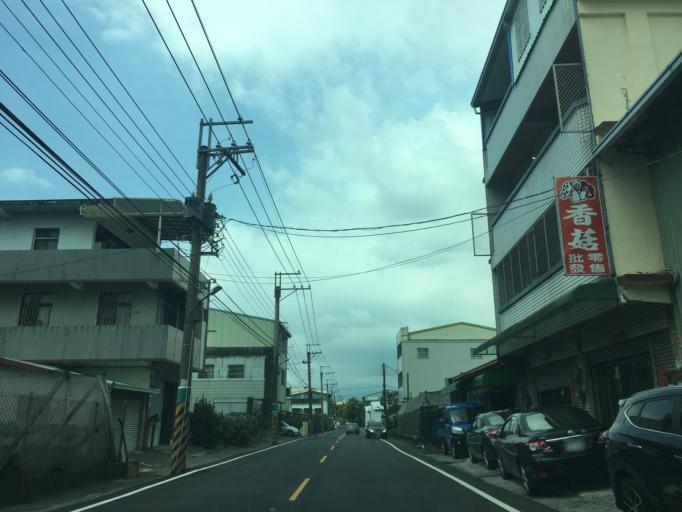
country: TW
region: Taiwan
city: Fengyuan
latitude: 24.2230
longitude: 120.7949
